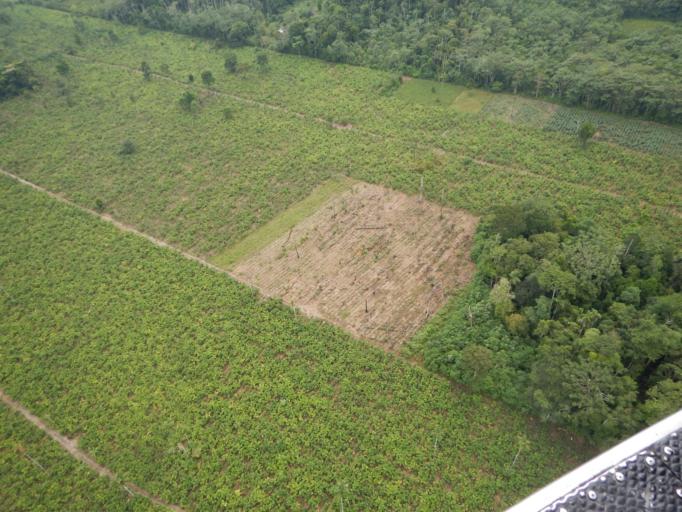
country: BO
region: Cochabamba
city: Chimore
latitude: -17.2162
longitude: -64.7074
